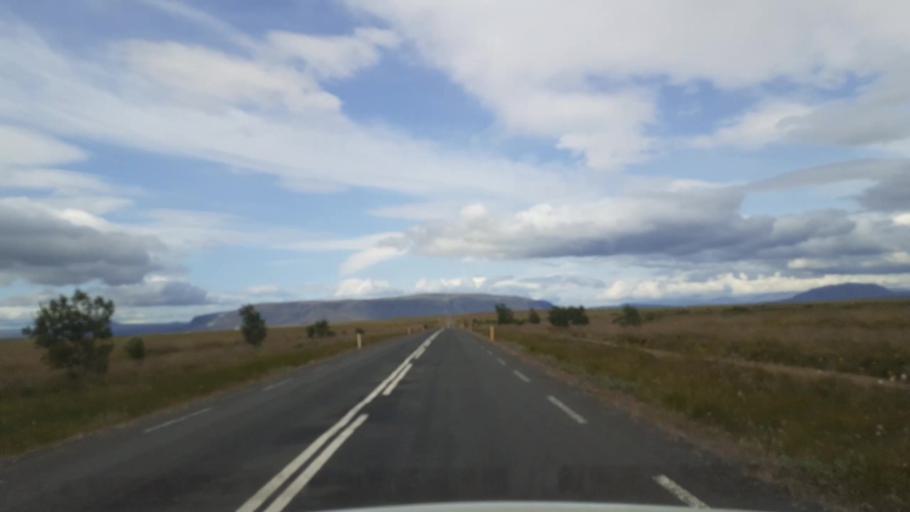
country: IS
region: South
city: Selfoss
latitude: 63.9088
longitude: -20.8248
